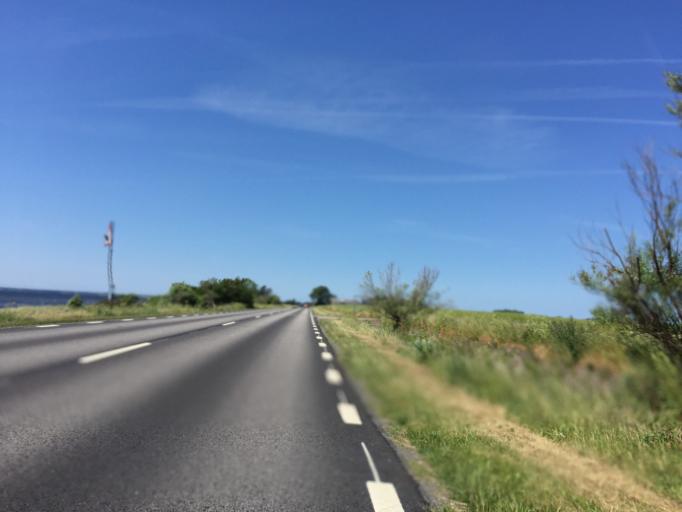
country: SE
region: Skane
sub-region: Trelleborgs Kommun
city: Skare
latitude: 55.3842
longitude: 13.0231
